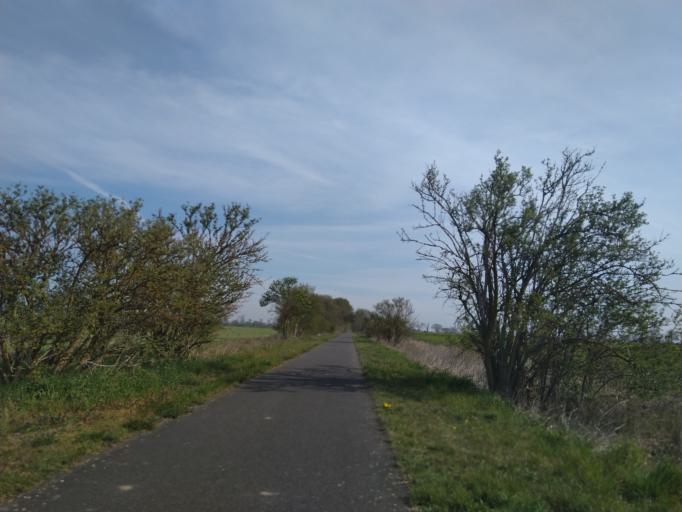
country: DE
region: Brandenburg
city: Wriezen
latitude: 52.7281
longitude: 14.1479
